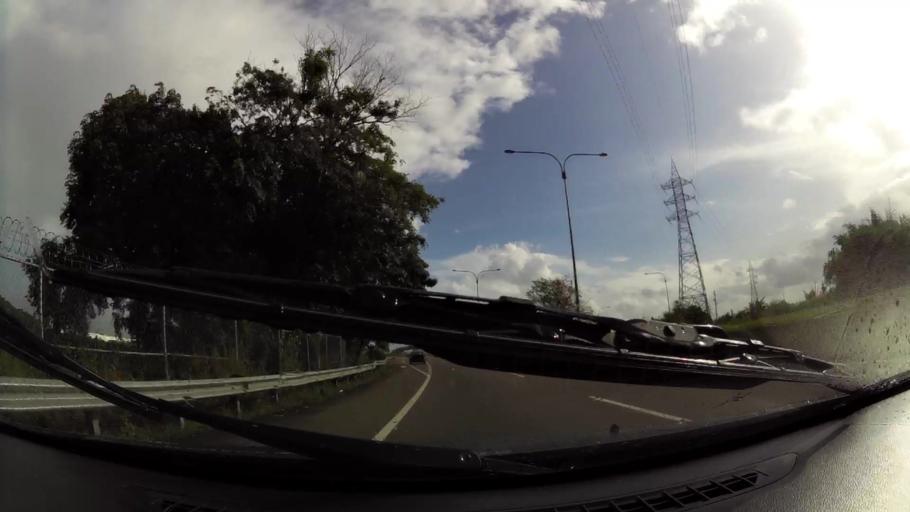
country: TT
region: Tunapuna/Piarco
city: Tunapuna
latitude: 10.6373
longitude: -61.4312
